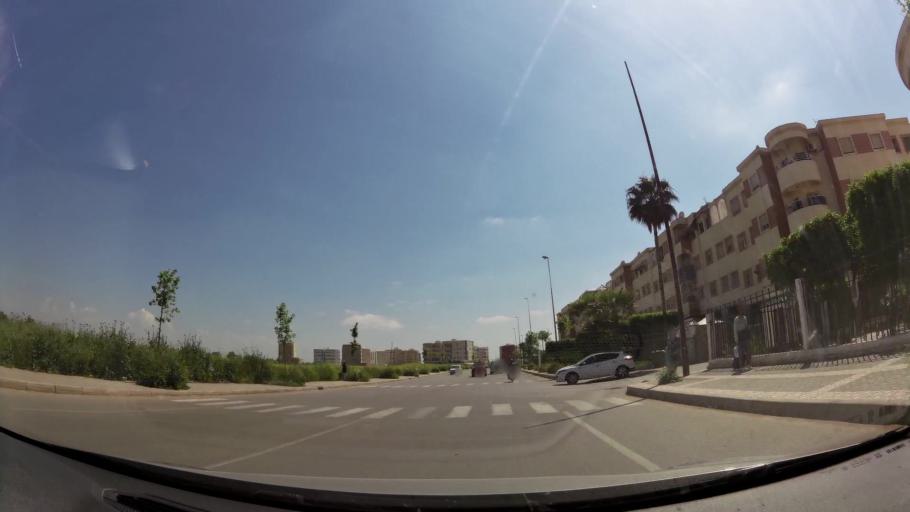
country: MA
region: Fes-Boulemane
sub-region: Fes
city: Fes
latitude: 34.0141
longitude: -5.0213
